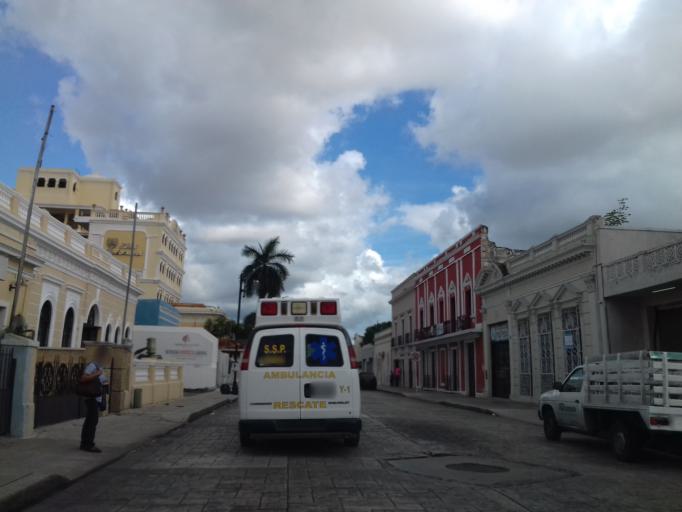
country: MX
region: Yucatan
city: Merida
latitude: 20.9706
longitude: -89.6347
